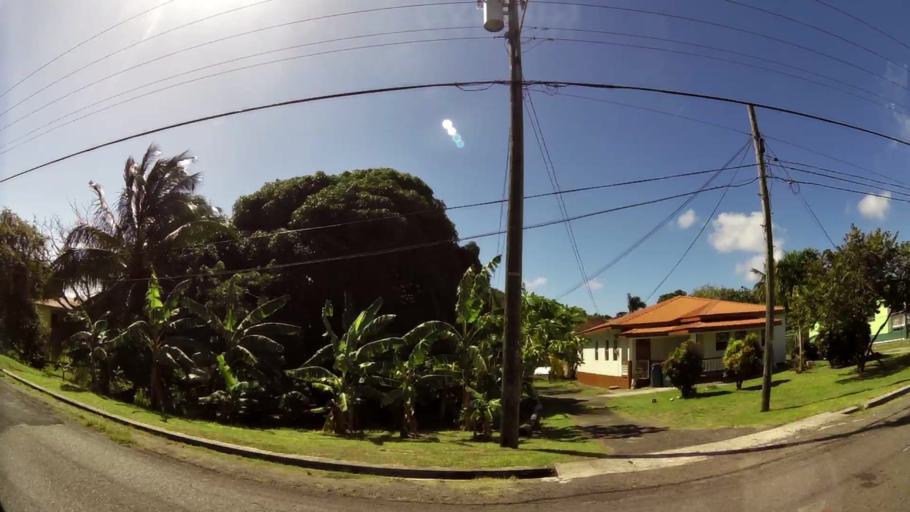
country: LC
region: Laborie Quarter
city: Laborie
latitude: 13.7482
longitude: -60.9628
